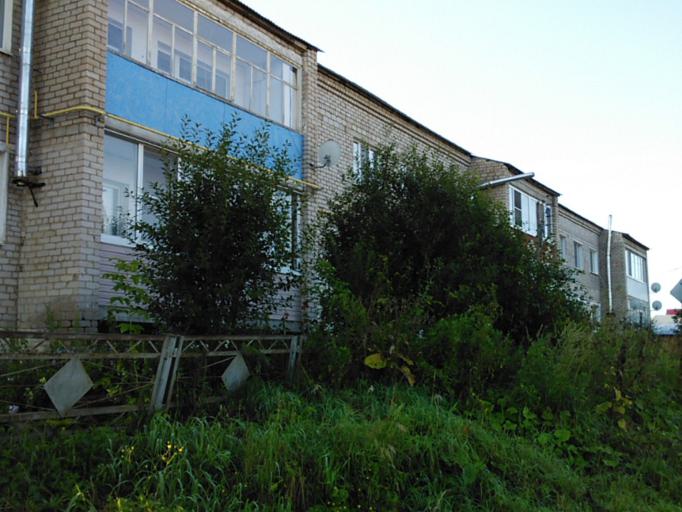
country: RU
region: Perm
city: Foki
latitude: 56.6987
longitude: 54.3550
